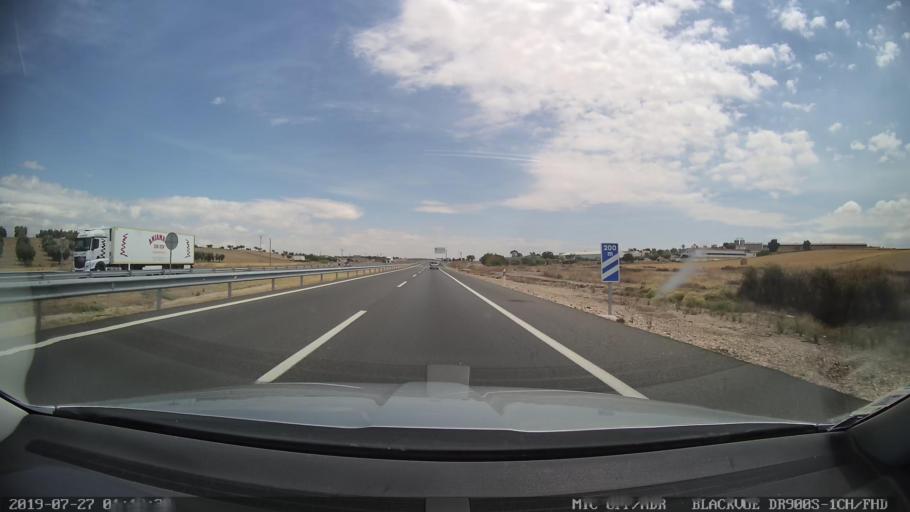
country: ES
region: Castille-La Mancha
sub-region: Province of Toledo
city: Santa Olalla
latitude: 40.0245
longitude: -4.4627
